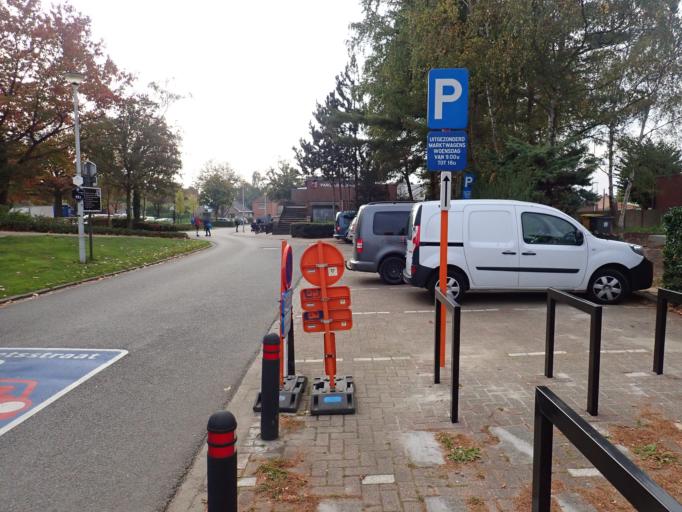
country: BE
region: Flanders
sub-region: Provincie Antwerpen
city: Nijlen
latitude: 51.1373
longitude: 4.6813
